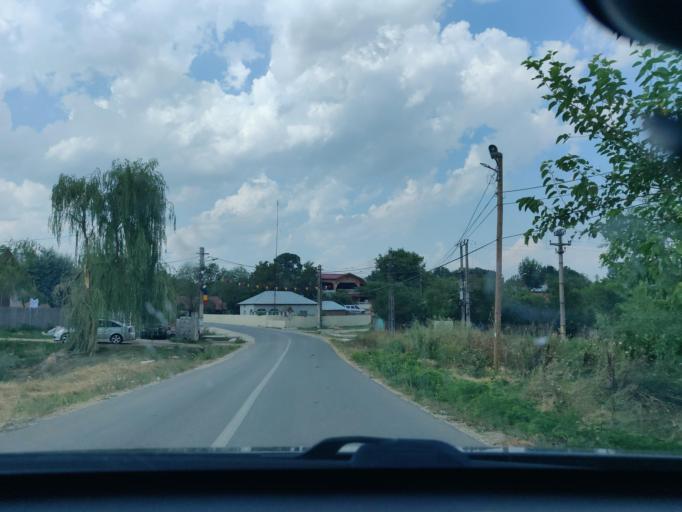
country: RO
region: Teleorman
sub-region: Comuna Sarbeni
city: Sarbeni
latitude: 44.4738
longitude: 25.3866
